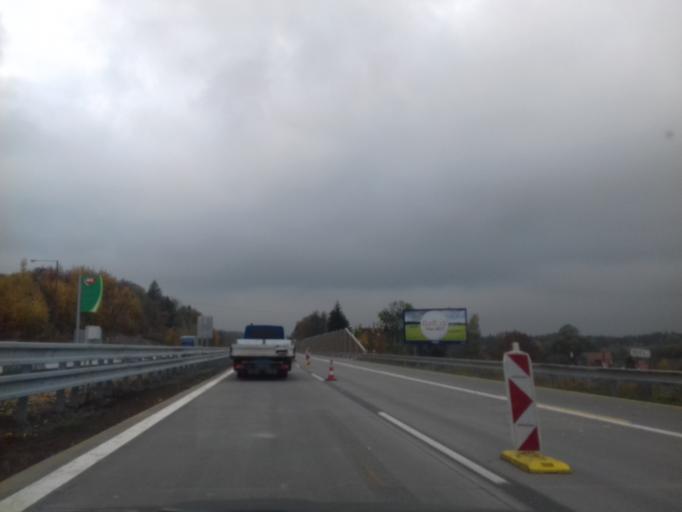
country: CZ
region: Central Bohemia
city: Ondrejov
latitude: 49.8411
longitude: 14.8134
